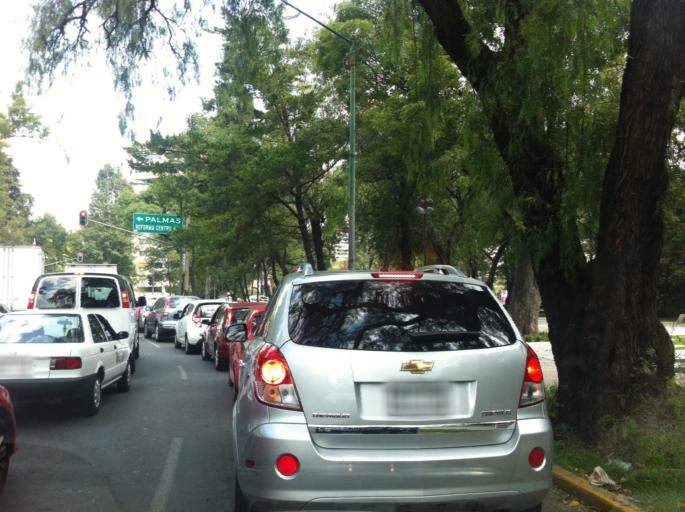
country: MX
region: Mexico City
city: Miguel Hidalgo
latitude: 19.4261
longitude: -99.1986
